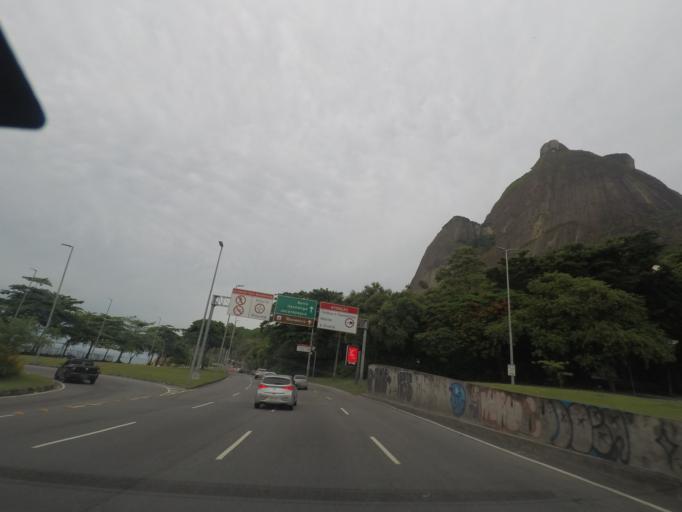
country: BR
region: Rio de Janeiro
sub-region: Rio De Janeiro
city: Rio de Janeiro
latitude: -22.9995
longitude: -43.2727
